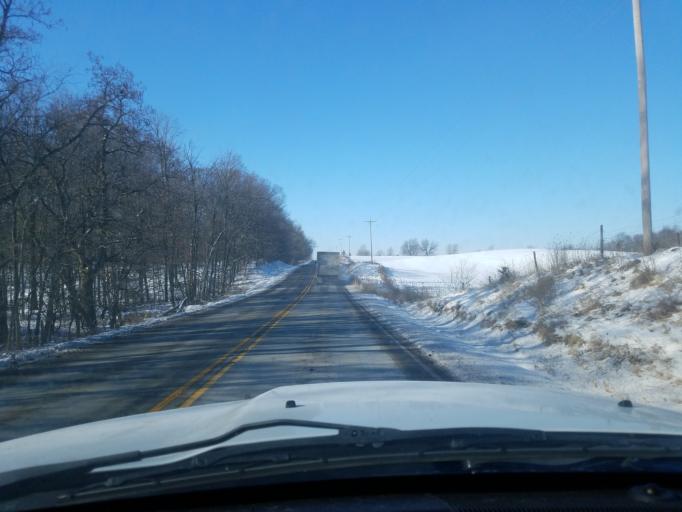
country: US
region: Indiana
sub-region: Noble County
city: Kendallville
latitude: 41.3951
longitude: -85.3139
